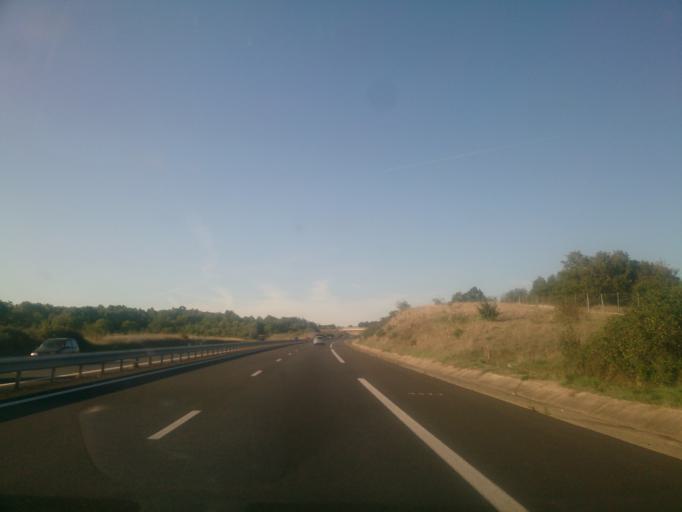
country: FR
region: Midi-Pyrenees
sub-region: Departement du Lot
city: Pradines
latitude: 44.5685
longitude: 1.5123
